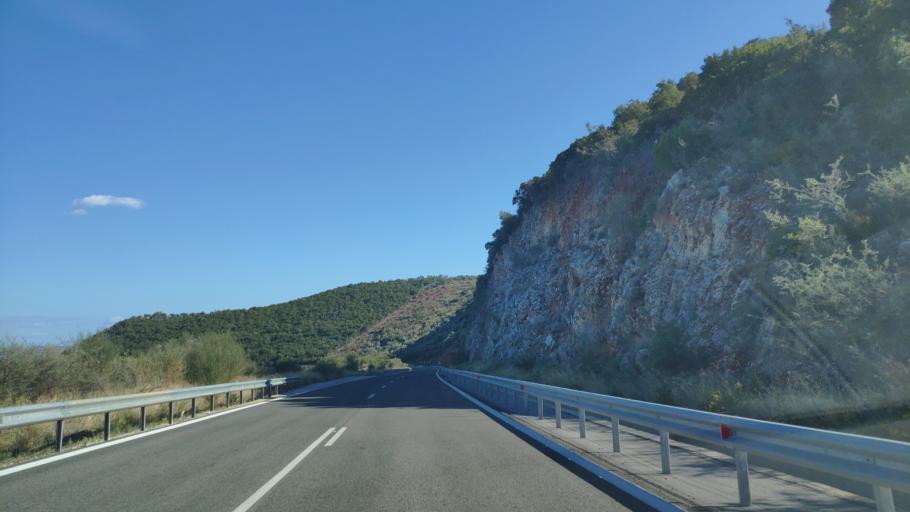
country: GR
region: Peloponnese
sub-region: Nomos Argolidos
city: Didyma
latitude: 37.5548
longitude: 23.2628
